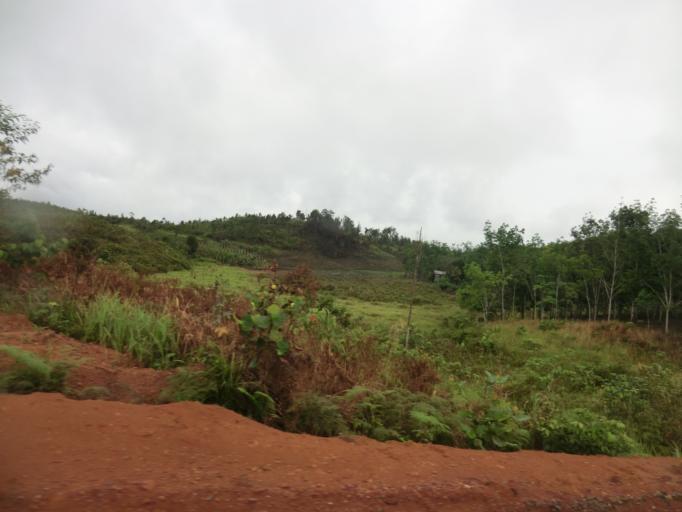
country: MY
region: Sarawak
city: Simanggang
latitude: 1.0724
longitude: 111.9654
